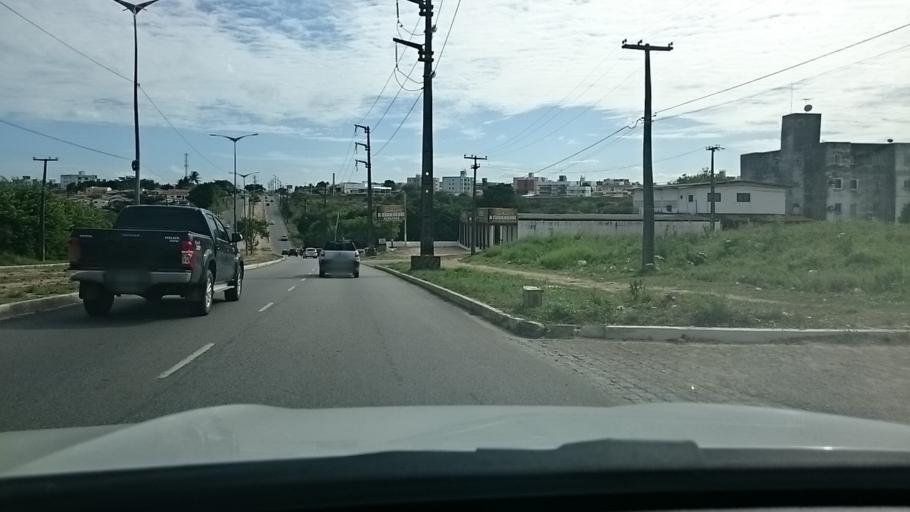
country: BR
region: Paraiba
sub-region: Joao Pessoa
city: Joao Pessoa
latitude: -7.1619
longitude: -34.8435
